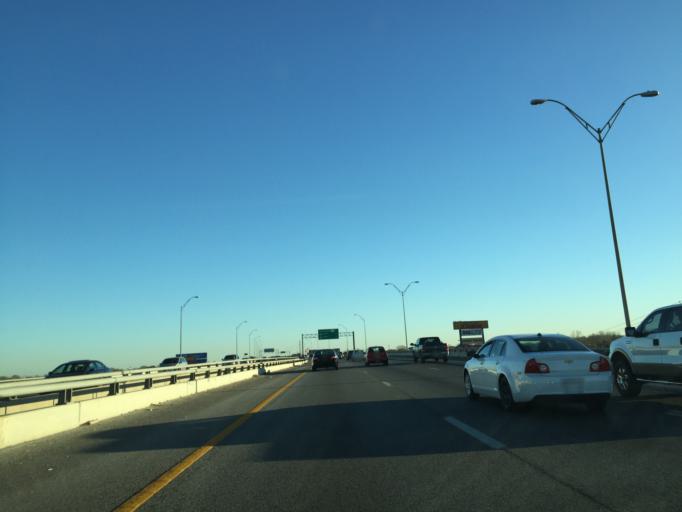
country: US
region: Texas
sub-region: Travis County
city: Wells Branch
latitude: 30.3665
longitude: -97.7183
